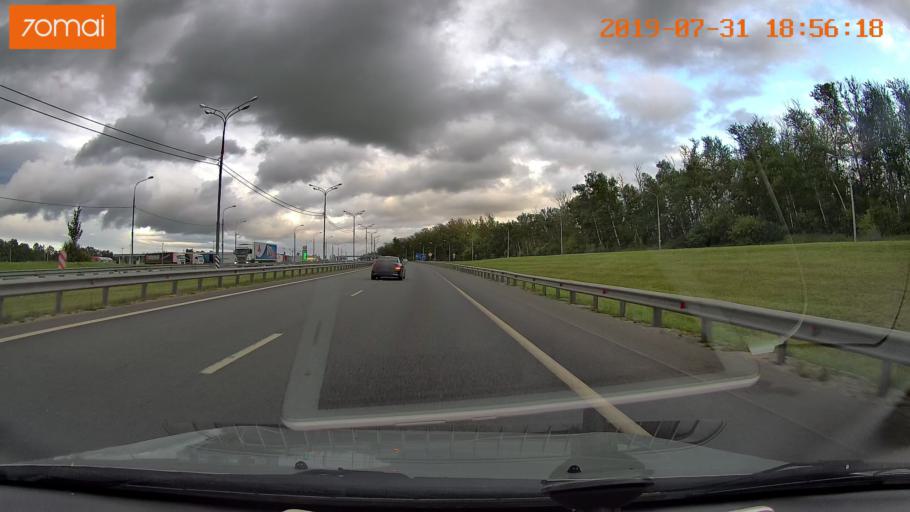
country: RU
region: Moskovskaya
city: Raduzhnyy
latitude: 55.1646
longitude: 38.6760
